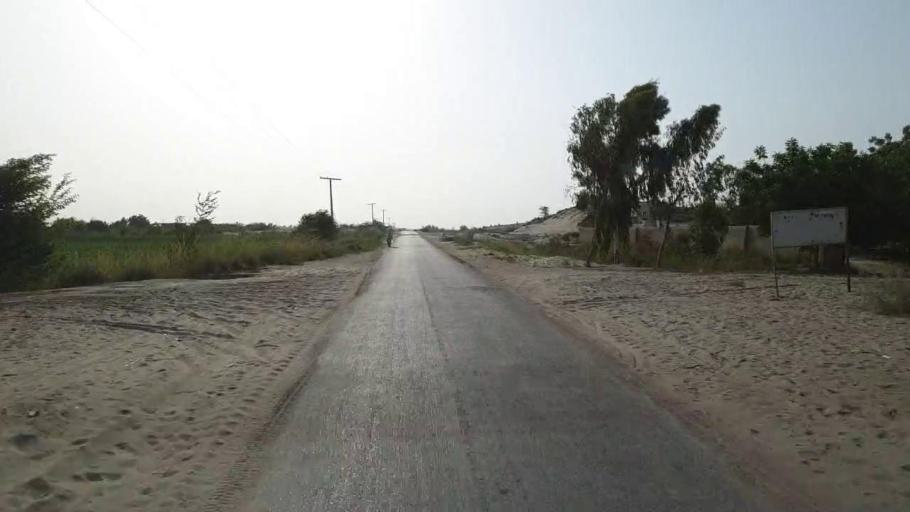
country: PK
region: Sindh
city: Jam Sahib
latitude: 26.4365
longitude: 68.8712
